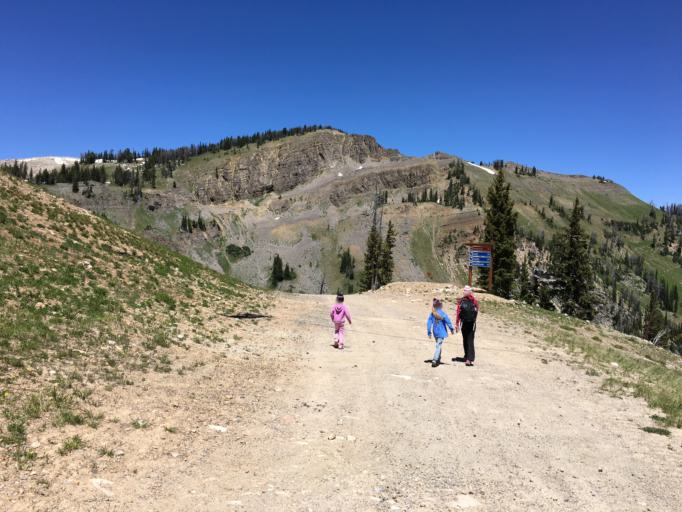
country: US
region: Wyoming
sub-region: Teton County
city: Moose Wilson Road
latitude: 43.5948
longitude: -110.8590
